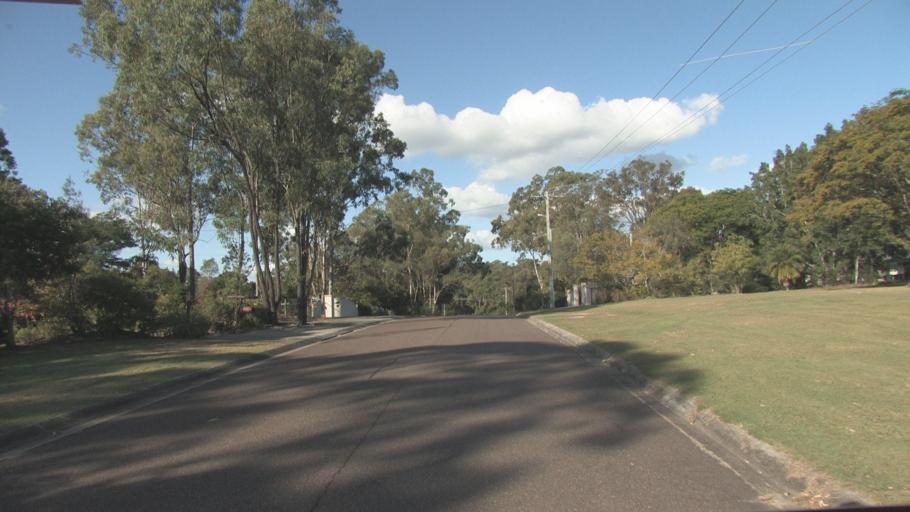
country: AU
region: Queensland
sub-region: Logan
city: Windaroo
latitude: -27.7588
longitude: 153.1949
